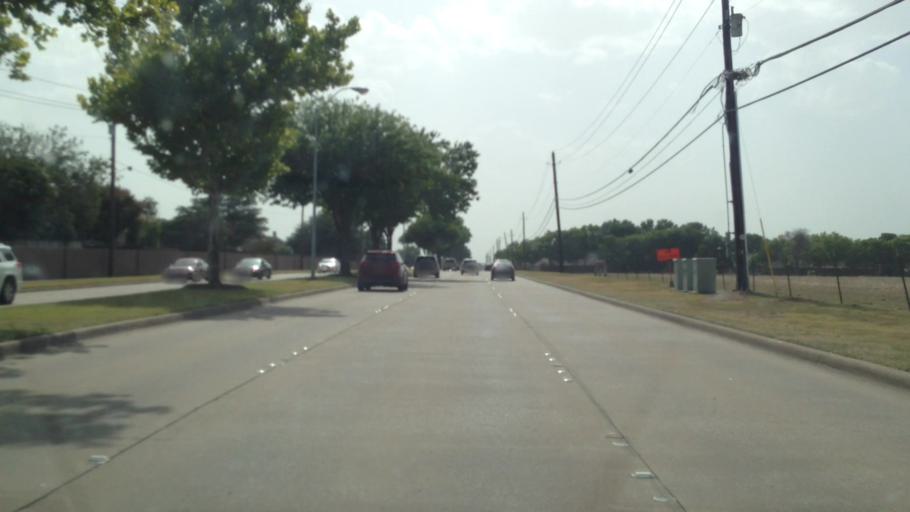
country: US
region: Texas
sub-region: Collin County
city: Plano
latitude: 33.0265
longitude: -96.7202
